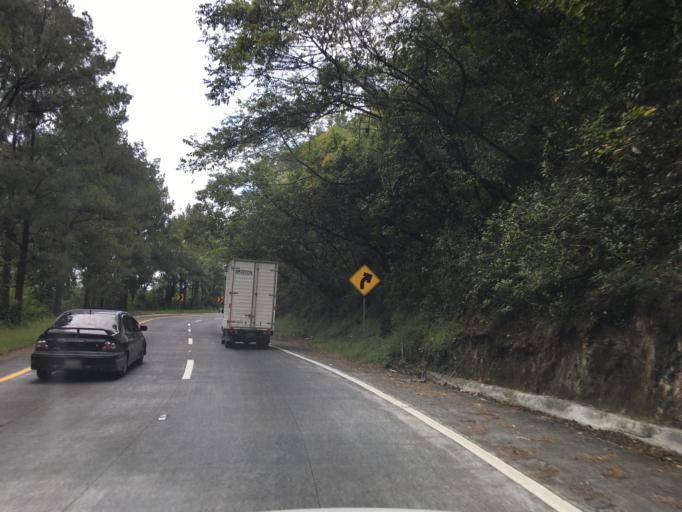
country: GT
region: Sacatepequez
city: Santa Lucia Milpas Altas
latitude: 14.5664
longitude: -90.6850
